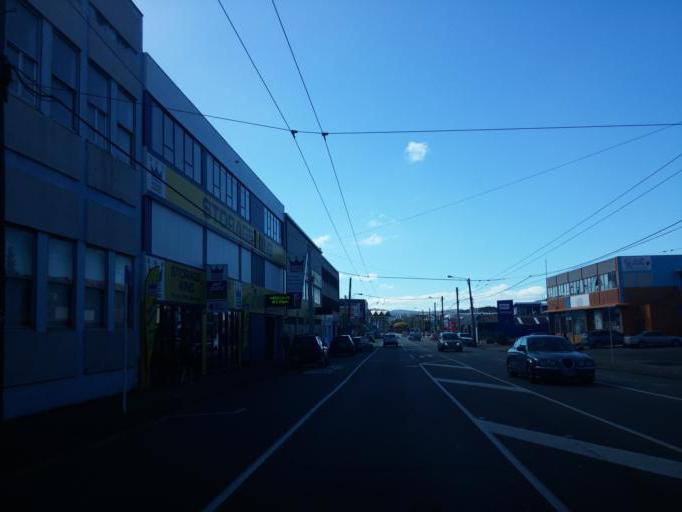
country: NZ
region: Wellington
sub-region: Wellington City
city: Wellington
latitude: -41.3047
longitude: 174.7786
